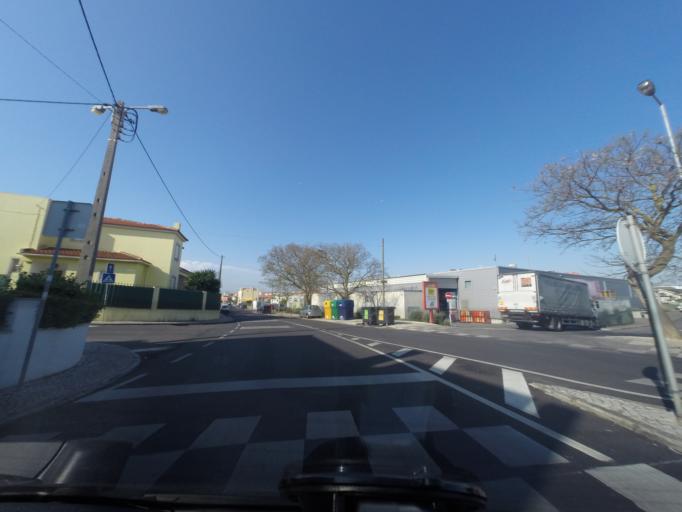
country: PT
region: Lisbon
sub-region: Cascais
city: Sao Domingos de Rana
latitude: 38.7167
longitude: -9.3435
